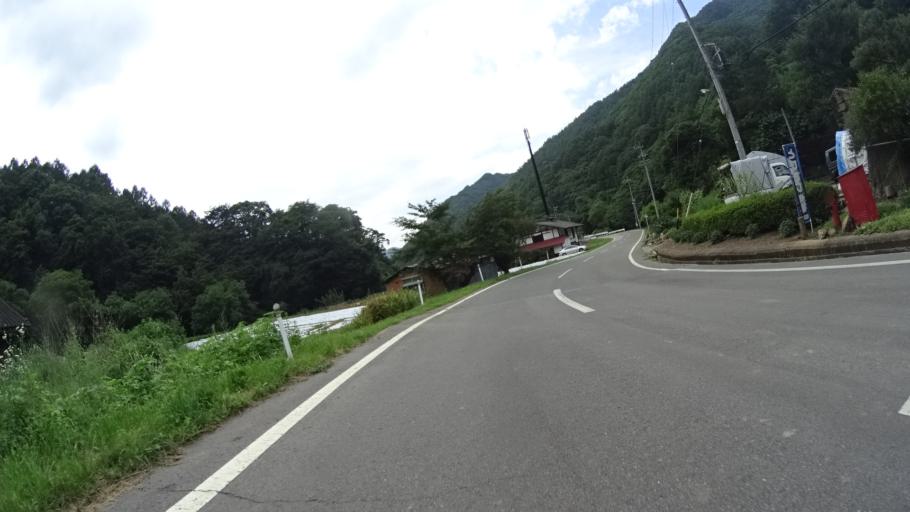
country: JP
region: Nagano
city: Saku
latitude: 36.0666
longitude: 138.5913
